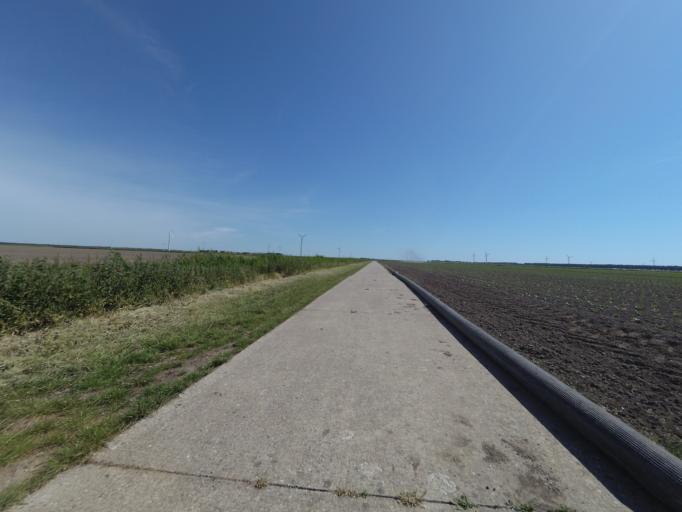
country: NL
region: North Holland
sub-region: Gemeente Huizen
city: Huizen
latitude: 52.3550
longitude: 5.3231
